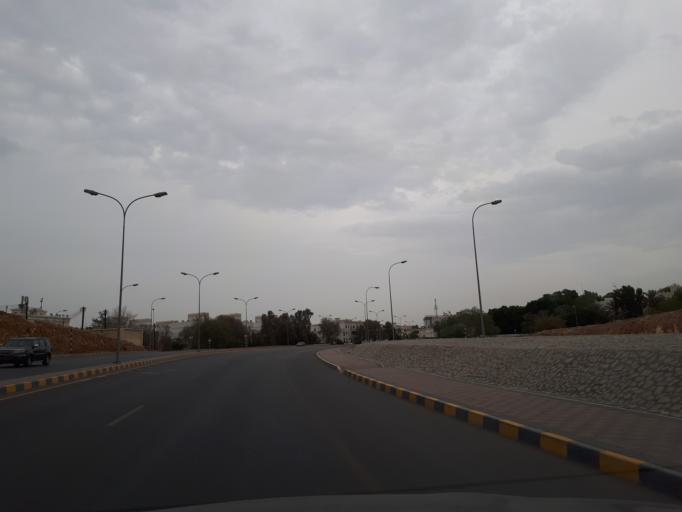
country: OM
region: Muhafazat Masqat
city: Bawshar
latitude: 23.5980
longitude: 58.4527
